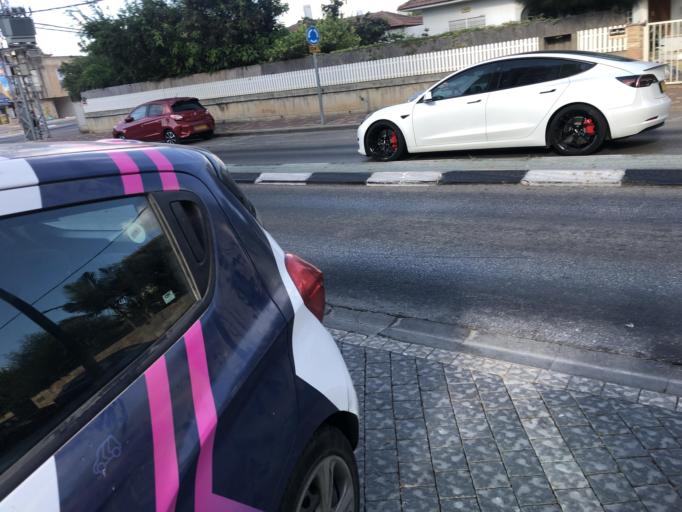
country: IL
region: Central District
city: Yehud
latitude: 32.0287
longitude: 34.8861
